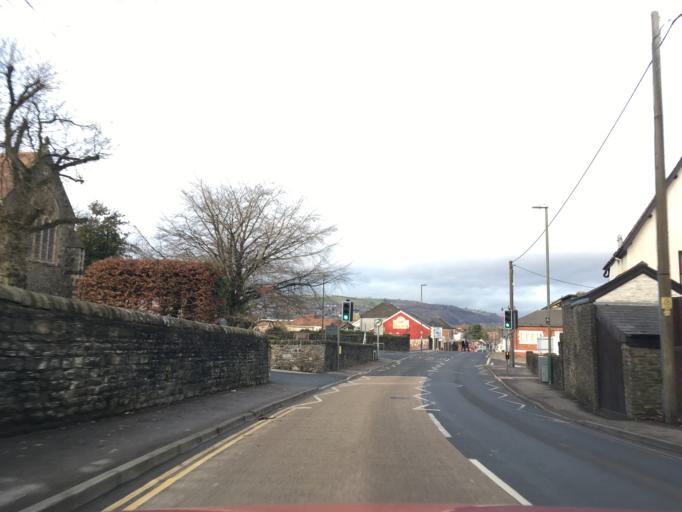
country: GB
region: Wales
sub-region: Caerphilly County Borough
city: Caerphilly
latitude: 51.5708
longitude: -3.2192
